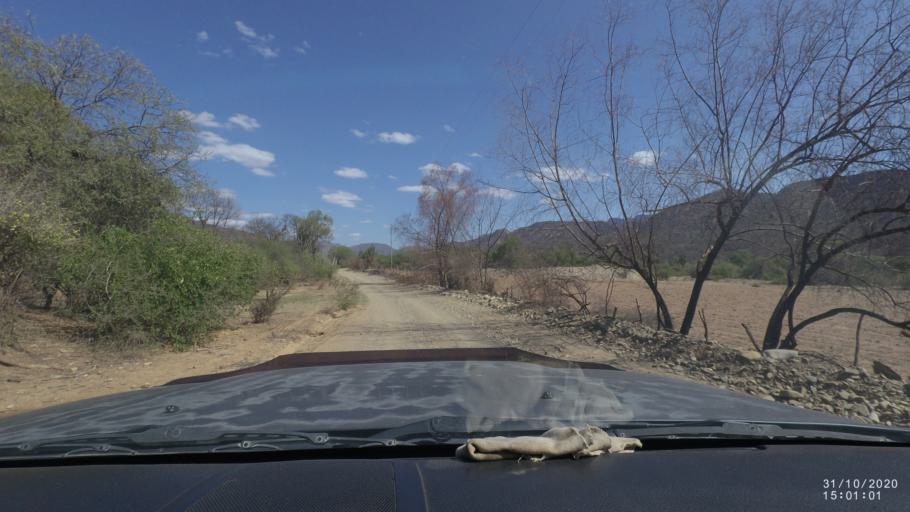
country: BO
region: Cochabamba
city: Aiquile
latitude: -18.2609
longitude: -64.8217
